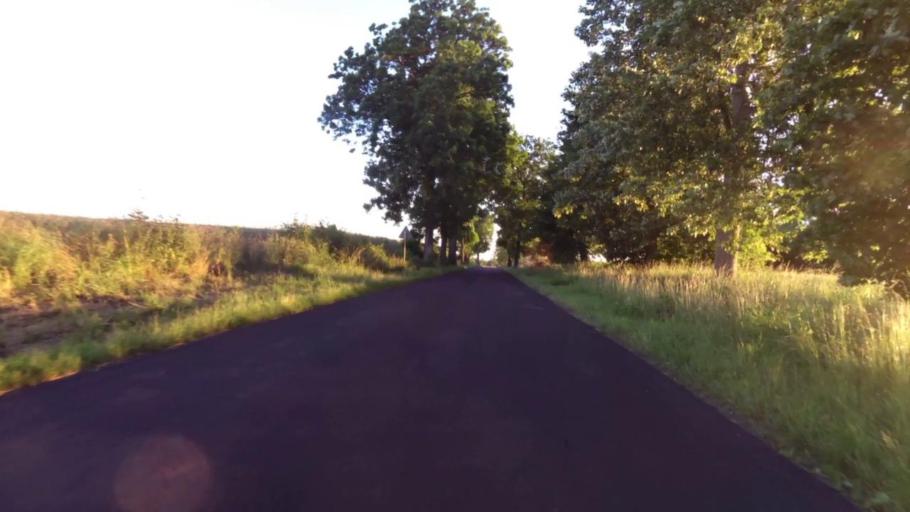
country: PL
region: West Pomeranian Voivodeship
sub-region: Powiat bialogardzki
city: Bialogard
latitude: 54.0270
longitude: 16.0266
